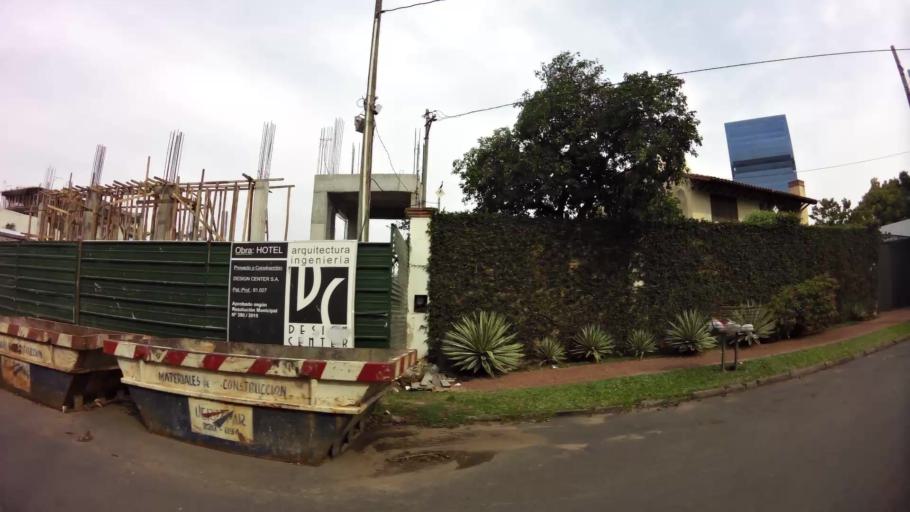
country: PY
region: Central
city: Fernando de la Mora
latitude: -25.2820
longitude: -57.5627
